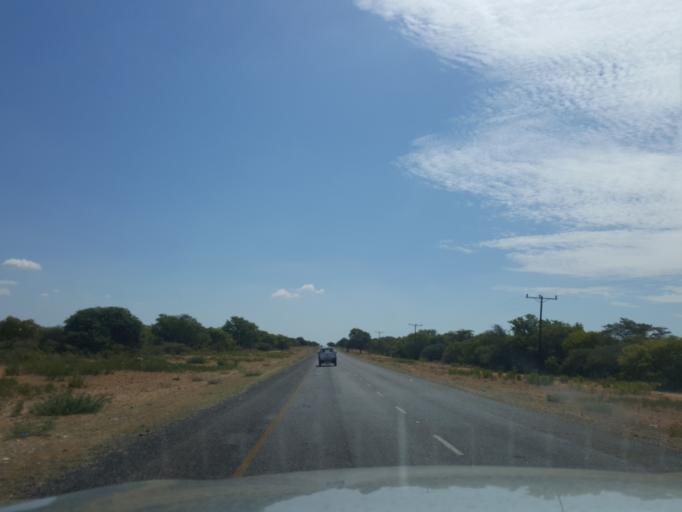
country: BW
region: Kweneng
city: Letlhakeng
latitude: -24.1249
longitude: 25.1040
